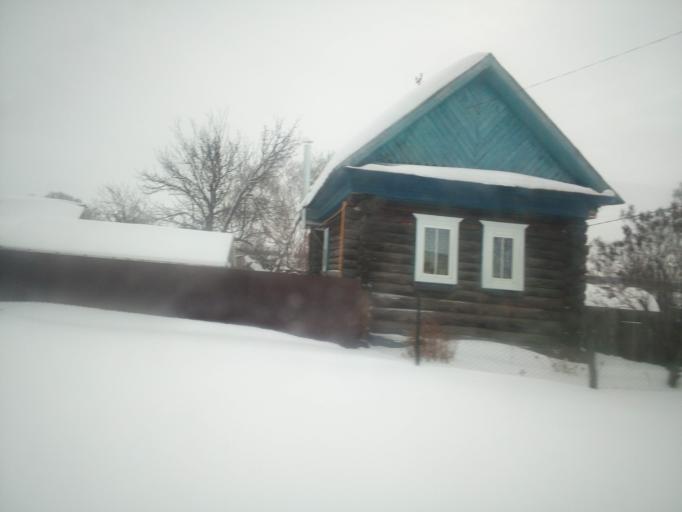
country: RU
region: Bashkortostan
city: Amzya
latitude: 56.1952
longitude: 54.3811
